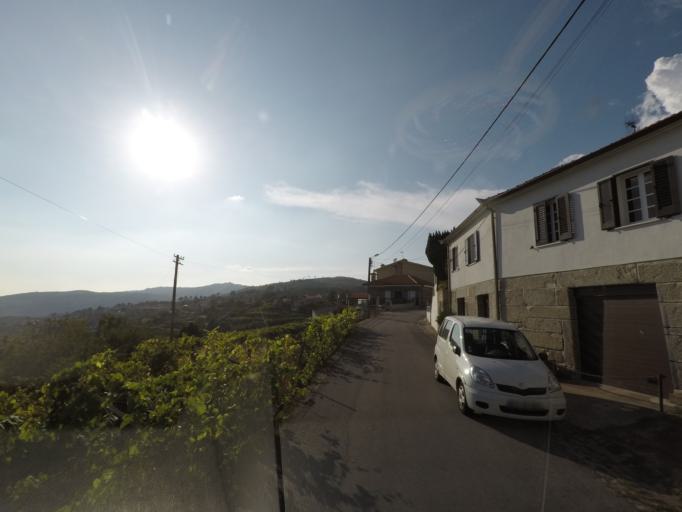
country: PT
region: Vila Real
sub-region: Mesao Frio
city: Mesao Frio
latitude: 41.1660
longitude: -7.9245
